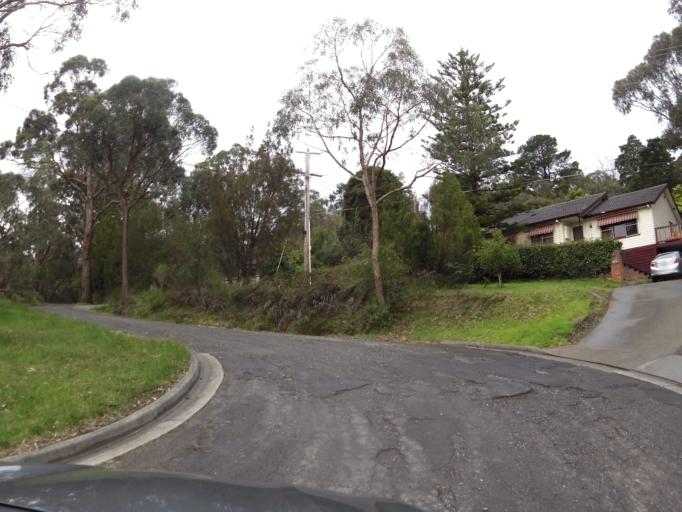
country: AU
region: Victoria
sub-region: Knox
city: Boronia
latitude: -37.8646
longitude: 145.2985
